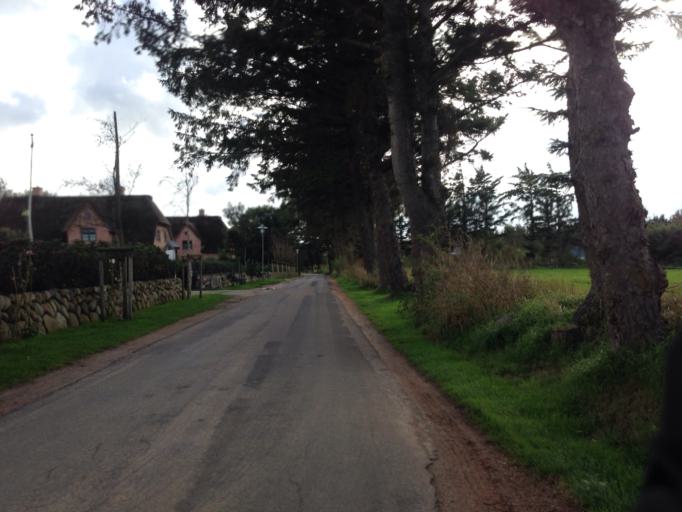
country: DE
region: Schleswig-Holstein
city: Utersum
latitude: 54.7102
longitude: 8.4017
